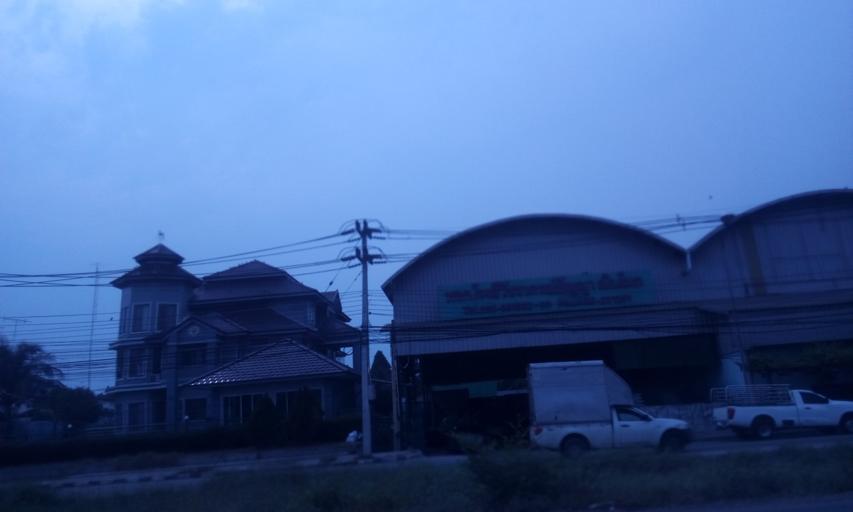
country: TH
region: Chon Buri
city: Ban Bueng
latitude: 13.2839
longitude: 101.2561
